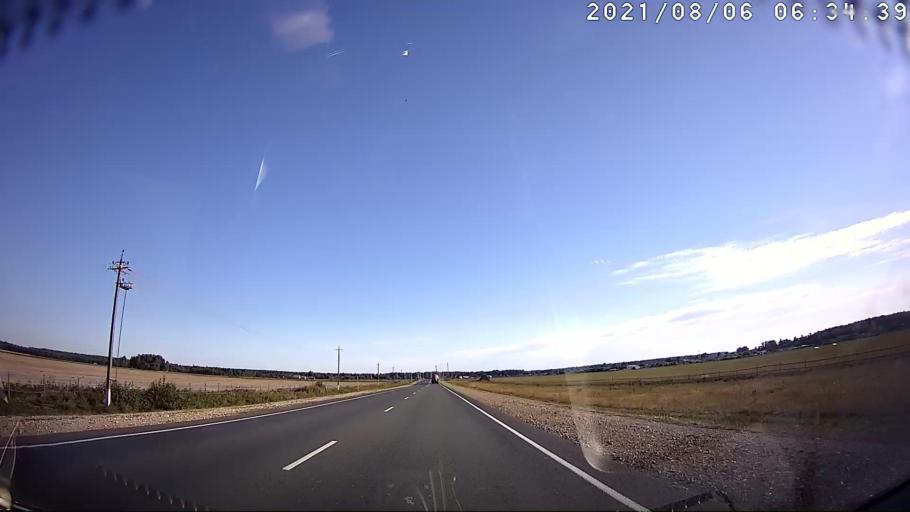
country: RU
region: Mariy-El
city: Krasnogorskiy
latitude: 56.2094
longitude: 48.2364
